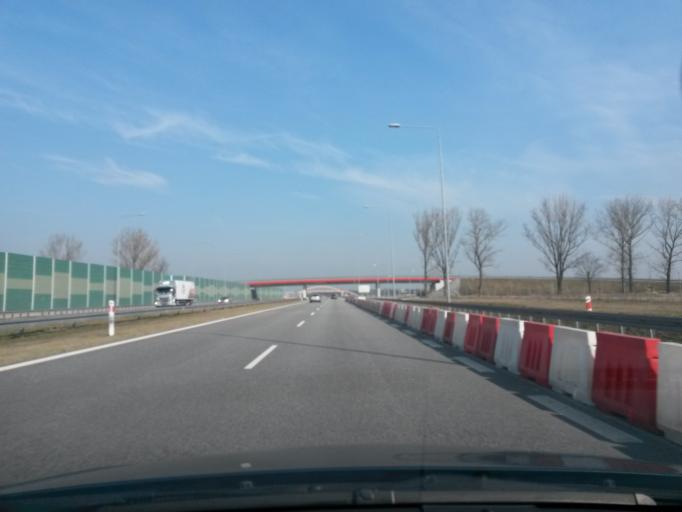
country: PL
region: Lodz Voivodeship
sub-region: Powiat kutnowski
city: Krzyzanow
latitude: 52.1801
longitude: 19.4869
